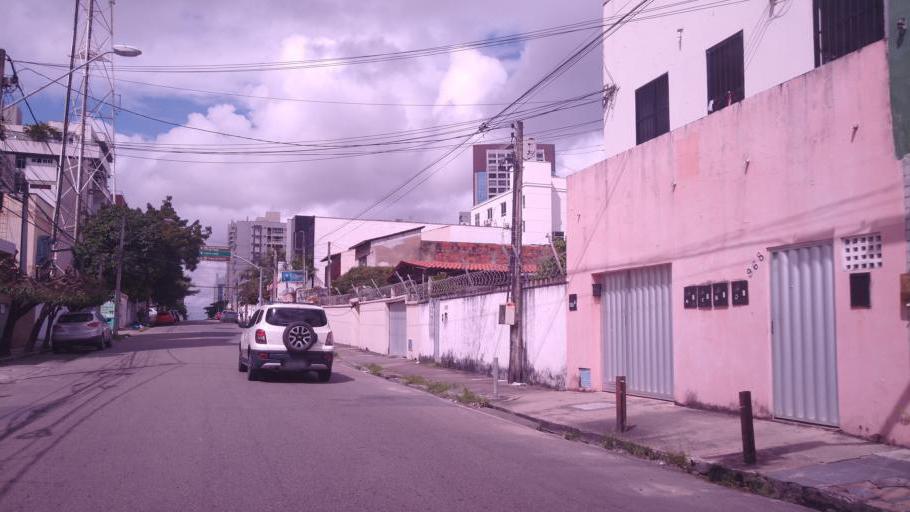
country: BR
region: Ceara
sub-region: Fortaleza
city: Fortaleza
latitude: -3.7327
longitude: -38.4887
